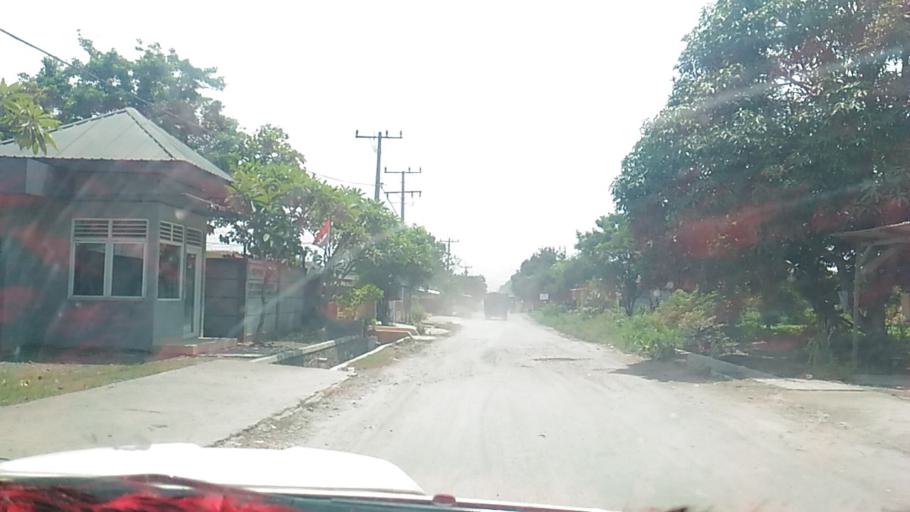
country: ID
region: North Sumatra
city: Sunggal
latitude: 3.5278
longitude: 98.5498
